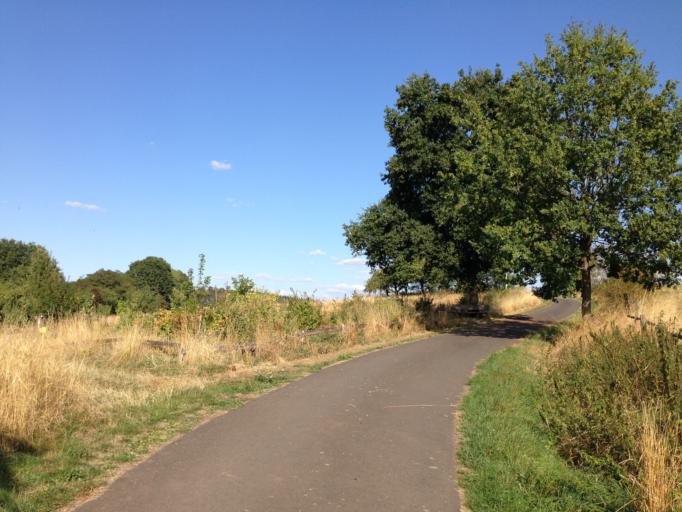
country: DE
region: Hesse
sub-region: Regierungsbezirk Giessen
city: Reiskirchen
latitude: 50.6191
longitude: 8.8575
